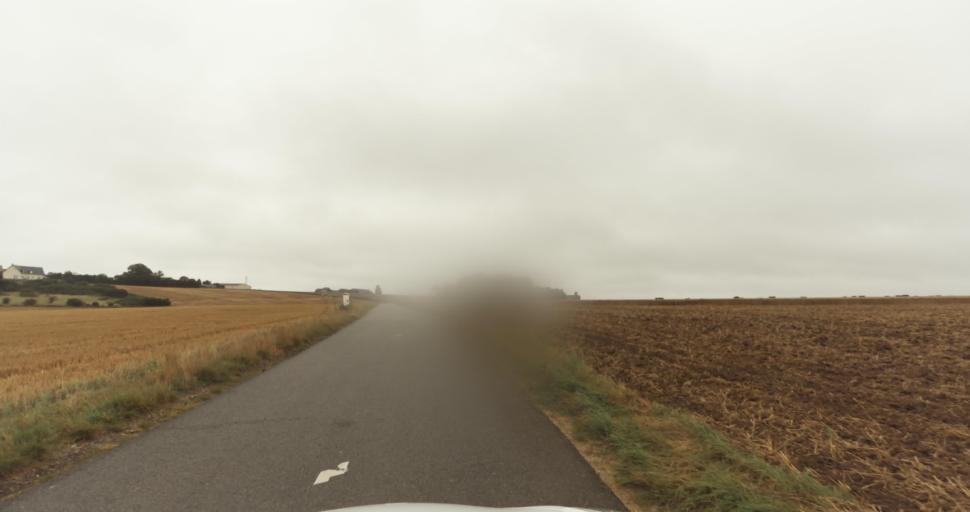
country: FR
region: Haute-Normandie
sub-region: Departement de l'Eure
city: Gravigny
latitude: 49.0775
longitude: 1.2168
